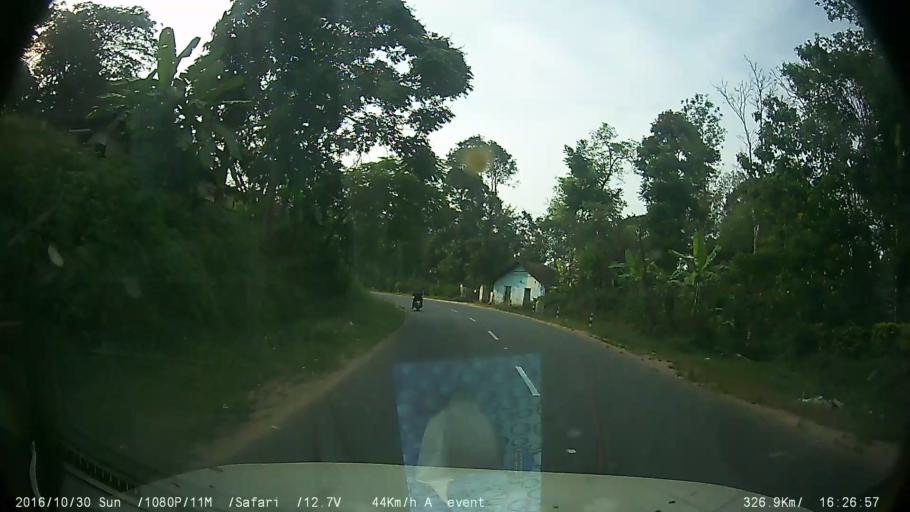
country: IN
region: Karnataka
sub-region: Kodagu
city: Suntikoppa
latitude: 12.4356
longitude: 75.8035
